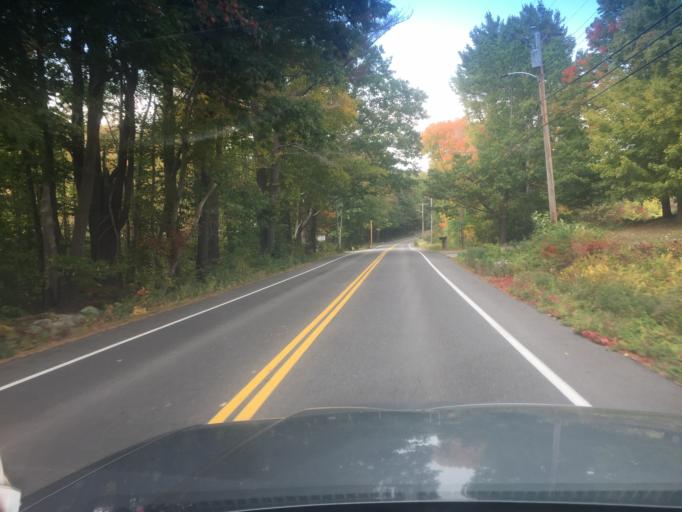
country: US
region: Maine
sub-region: York County
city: York Harbor
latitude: 43.1615
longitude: -70.6394
